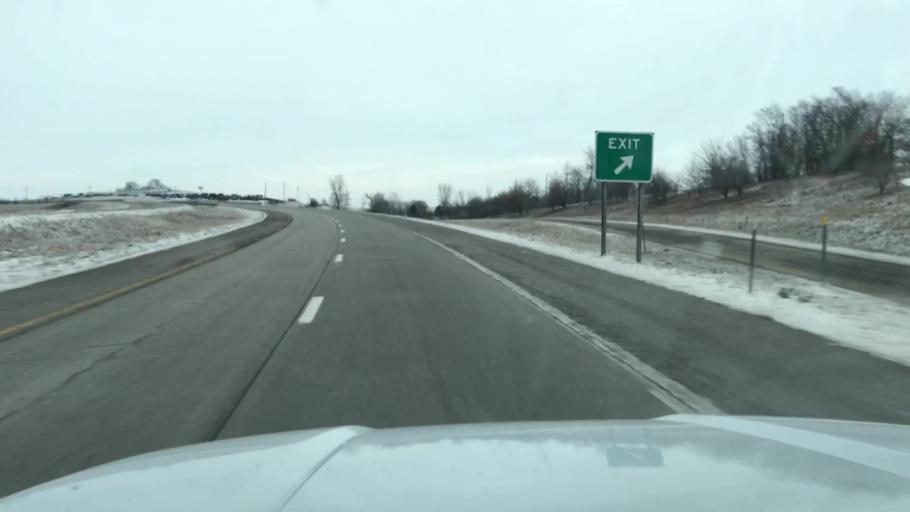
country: US
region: Missouri
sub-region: Andrew County
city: Savannah
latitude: 39.9582
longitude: -94.8600
